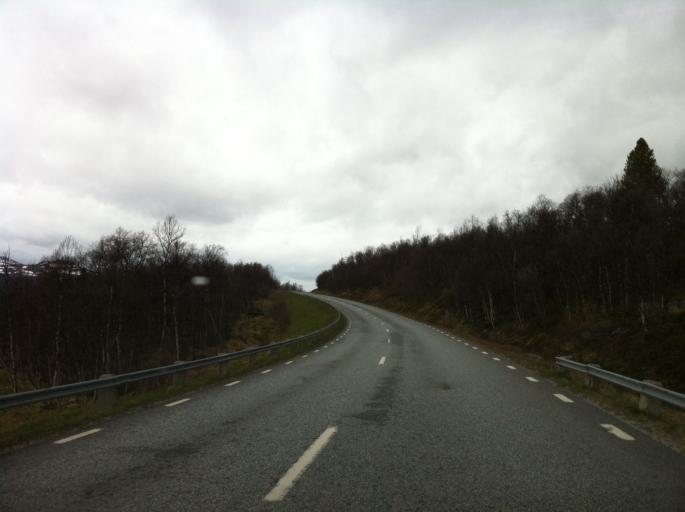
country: NO
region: Sor-Trondelag
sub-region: Tydal
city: Aas
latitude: 62.5990
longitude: 12.1792
